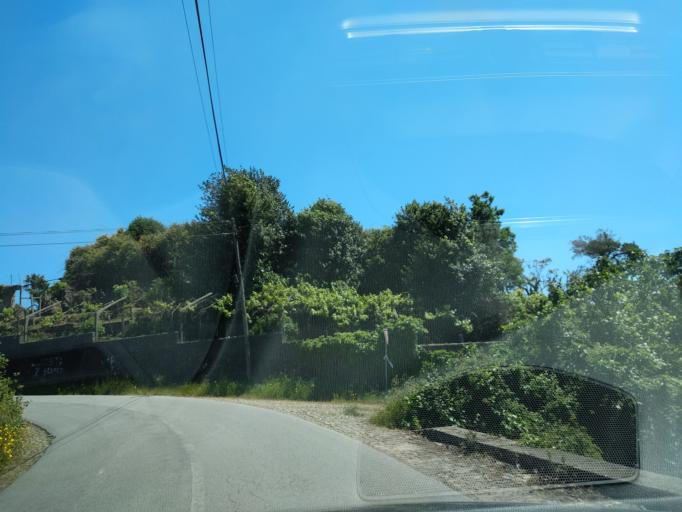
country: PT
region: Porto
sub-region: Paredes
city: Gandra
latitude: 41.1850
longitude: -8.4258
